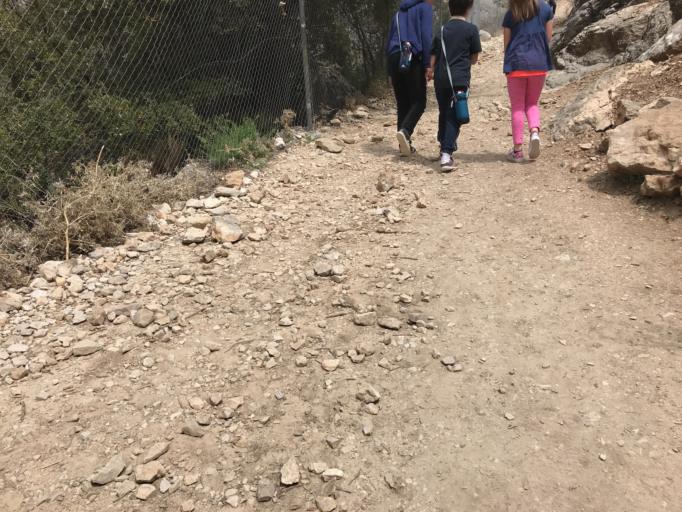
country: ES
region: Andalusia
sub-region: Provincia de Granada
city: Castril
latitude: 37.8936
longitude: -2.7484
